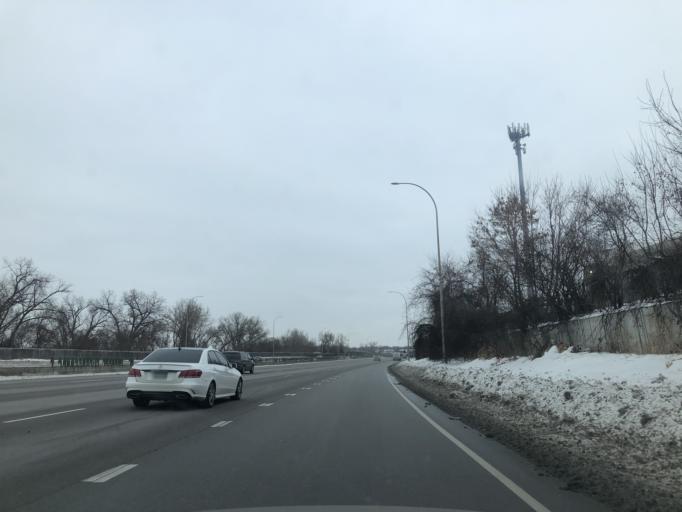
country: US
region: Minnesota
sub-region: Anoka County
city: Columbia Heights
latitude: 45.0394
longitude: -93.2853
